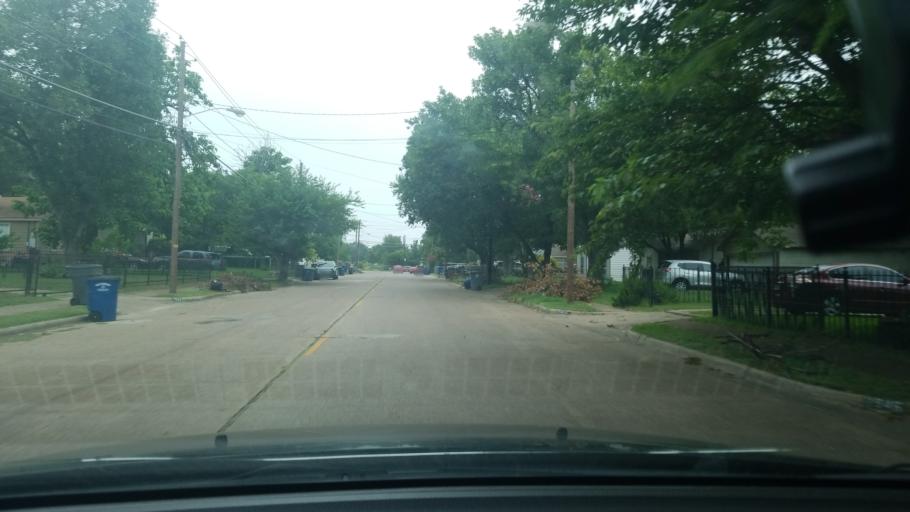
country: US
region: Texas
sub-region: Dallas County
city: Balch Springs
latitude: 32.7618
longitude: -96.6728
